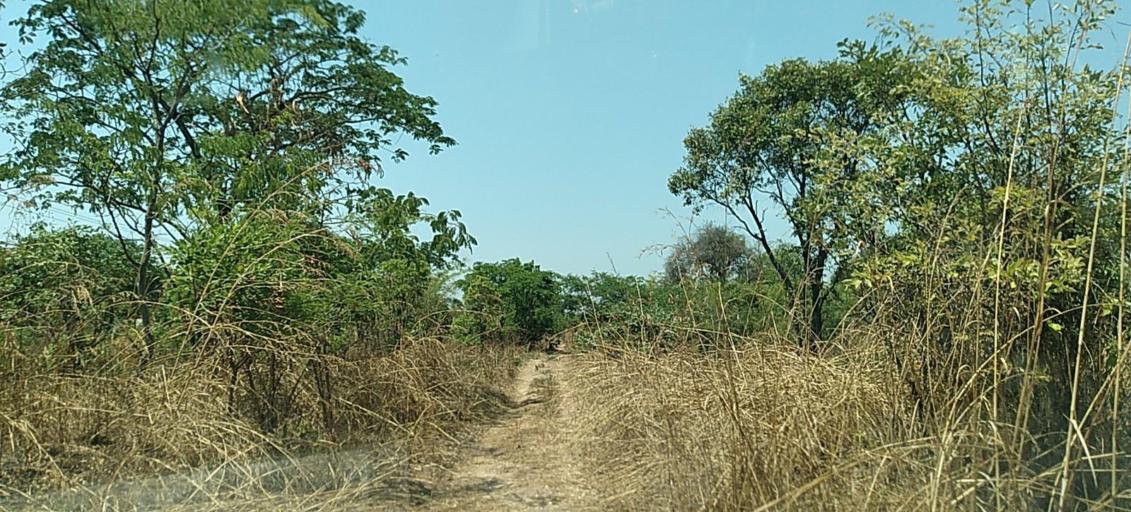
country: ZM
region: Copperbelt
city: Luanshya
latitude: -12.9813
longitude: 28.3290
